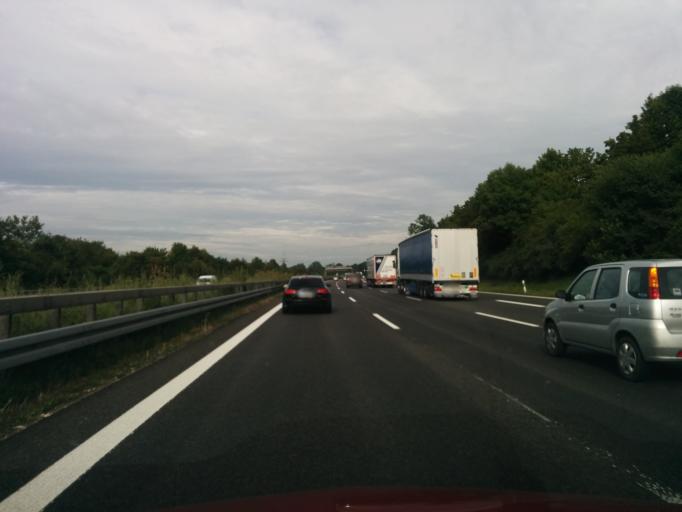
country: DE
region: Baden-Wuerttemberg
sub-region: Regierungsbezirk Stuttgart
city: Kirchheim unter Teck
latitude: 48.6307
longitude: 9.4613
